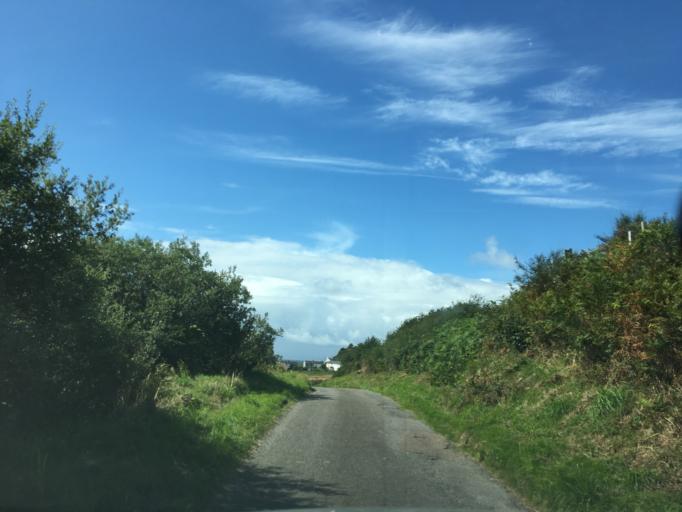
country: GB
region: Scotland
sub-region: Argyll and Bute
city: Isle Of Mull
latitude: 56.2477
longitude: -5.6428
